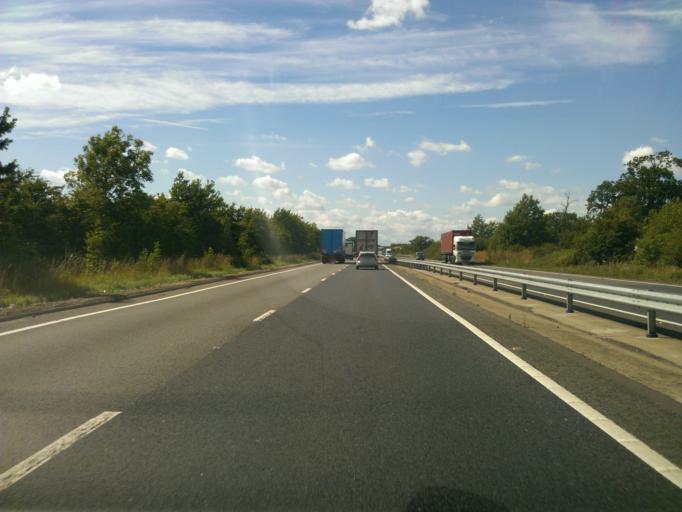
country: GB
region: England
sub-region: Bedford
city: Pertenhall
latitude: 52.3555
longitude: -0.3920
